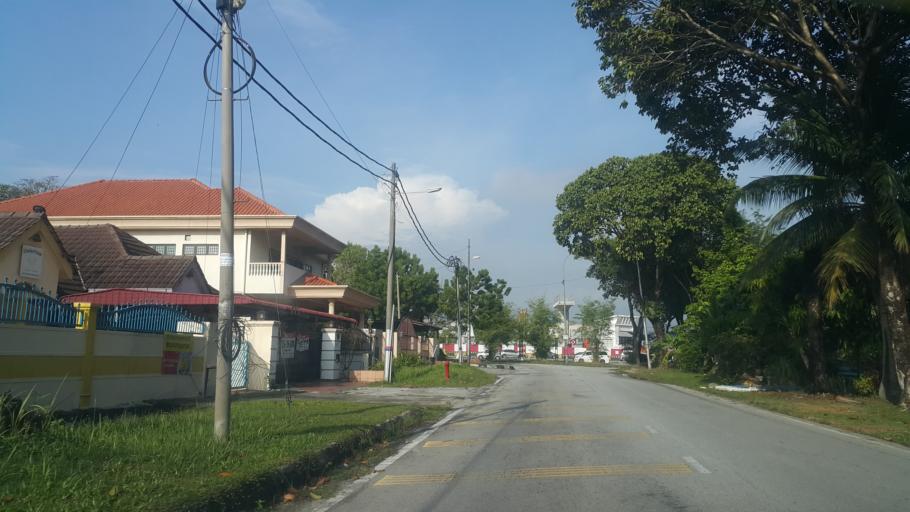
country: MY
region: Selangor
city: Klang
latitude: 3.0124
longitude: 101.4410
